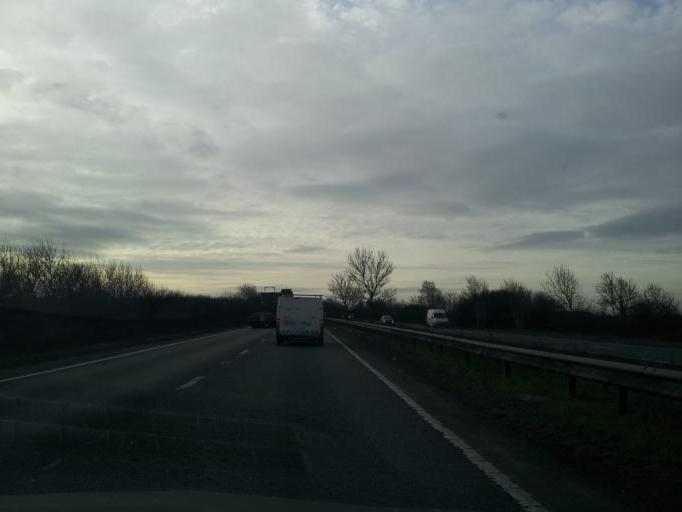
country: GB
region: England
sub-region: District of Rutland
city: Greetham
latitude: 52.7565
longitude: -0.6082
